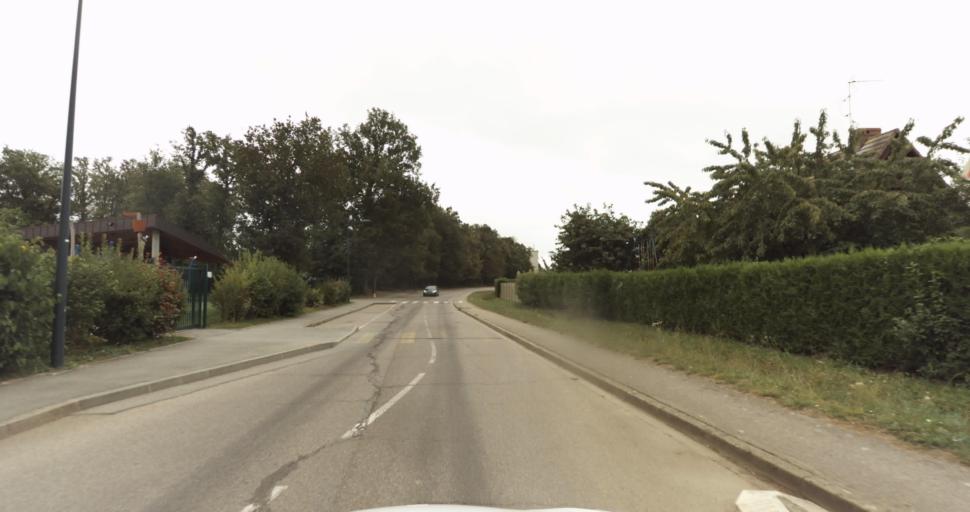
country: FR
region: Haute-Normandie
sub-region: Departement de l'Eure
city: Gravigny
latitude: 49.0311
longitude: 1.1787
